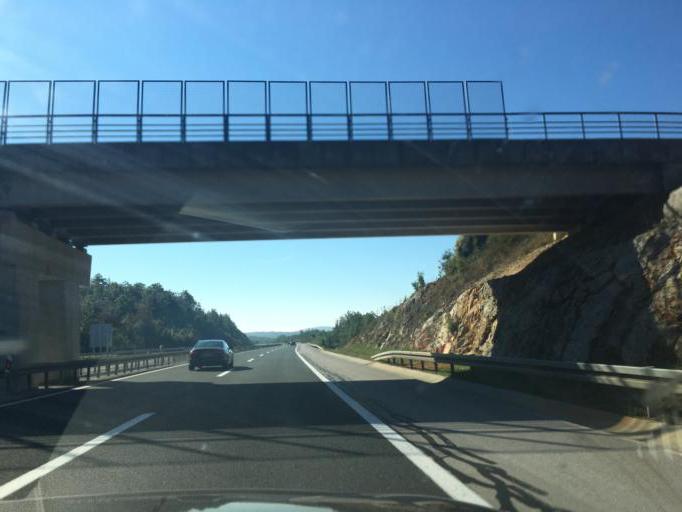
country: HR
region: Licko-Senjska
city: Otocac
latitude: 44.7438
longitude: 15.3779
